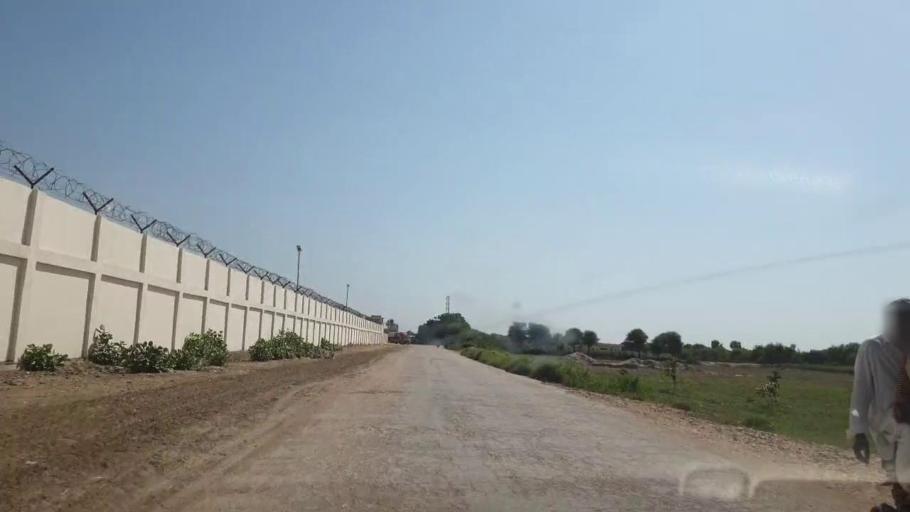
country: PK
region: Sindh
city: Tando Jam
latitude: 25.3851
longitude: 68.5791
